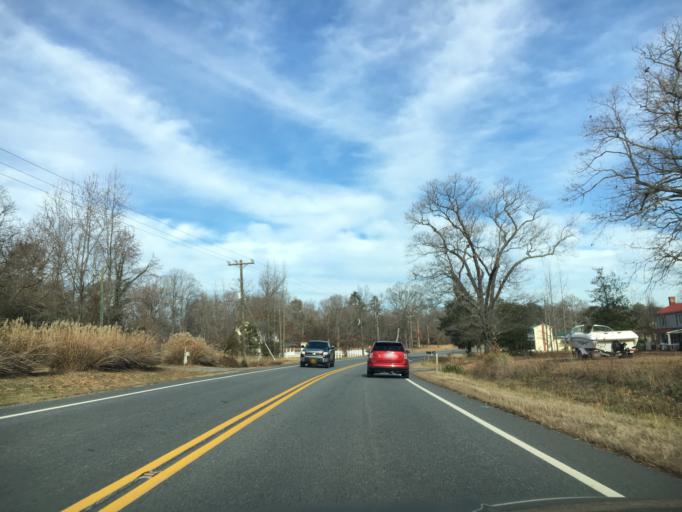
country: US
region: Virginia
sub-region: Louisa County
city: Louisa
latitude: 38.0402
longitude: -77.8868
